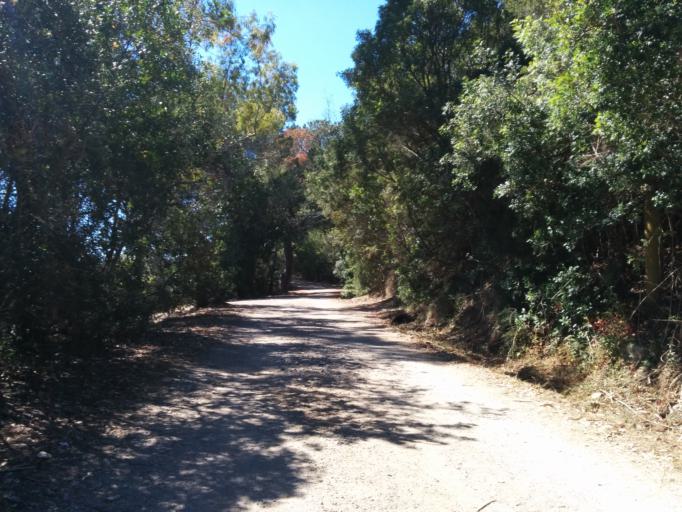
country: IT
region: Tuscany
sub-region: Provincia di Livorno
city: Portoferraio
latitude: 42.7553
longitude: 10.3186
